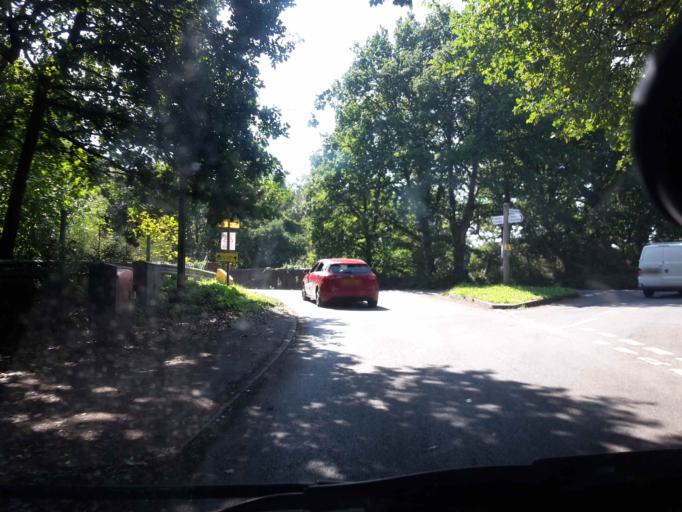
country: GB
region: England
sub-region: Surrey
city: Chilworth
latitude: 51.2130
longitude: -0.4647
